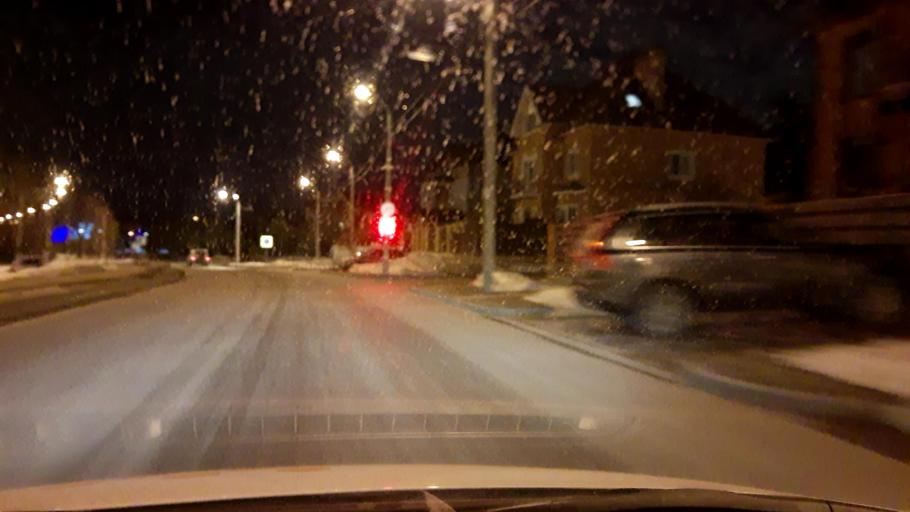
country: RU
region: Moskovskaya
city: Kommunarka
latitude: 55.5314
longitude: 37.4906
